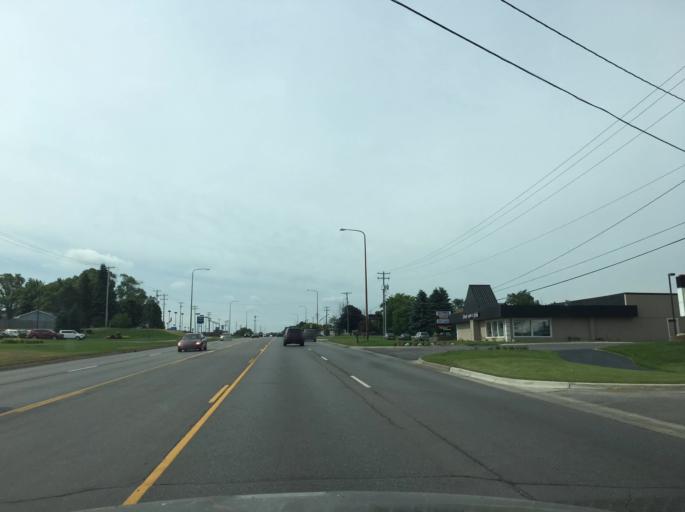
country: US
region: Michigan
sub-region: Grand Traverse County
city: Traverse City
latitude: 44.7288
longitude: -85.6462
